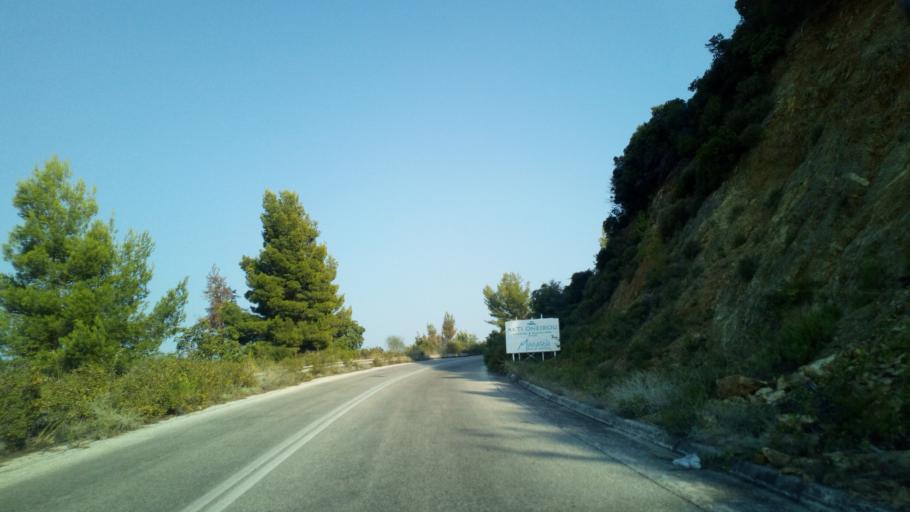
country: GR
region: Central Macedonia
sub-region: Nomos Chalkidikis
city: Neos Marmaras
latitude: 40.1726
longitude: 23.8581
